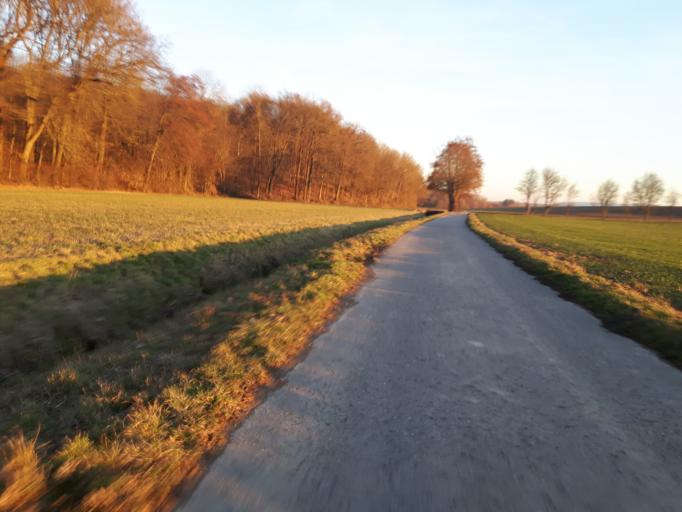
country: DE
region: Baden-Wuerttemberg
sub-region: Regierungsbezirk Stuttgart
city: Massenbachhausen
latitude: 49.1891
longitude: 9.0480
